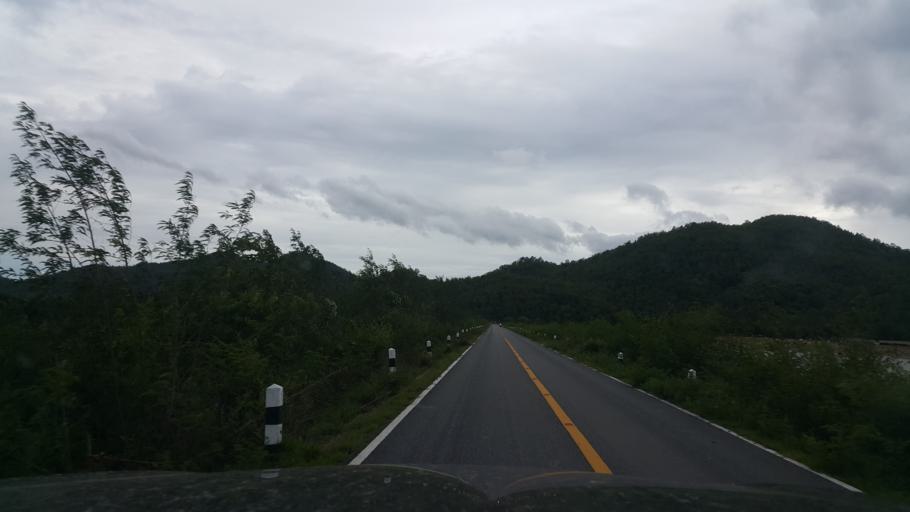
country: TH
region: Sukhothai
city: Thung Saliam
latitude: 17.1779
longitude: 99.4819
